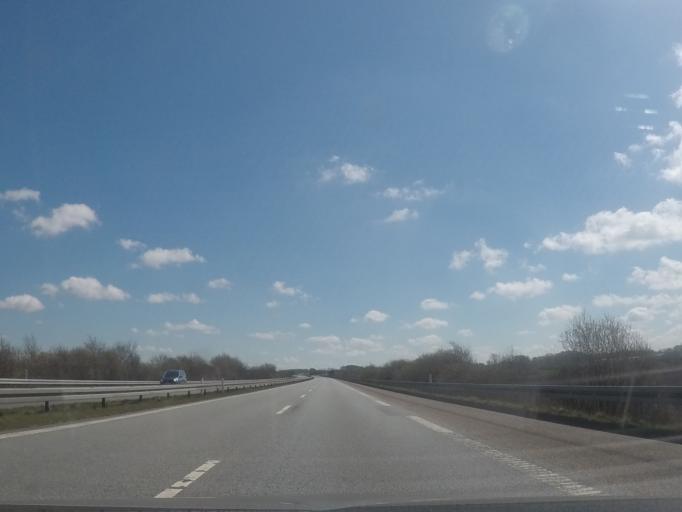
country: DK
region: South Denmark
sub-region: Kolding Kommune
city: Kolding
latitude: 55.5373
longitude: 9.5028
